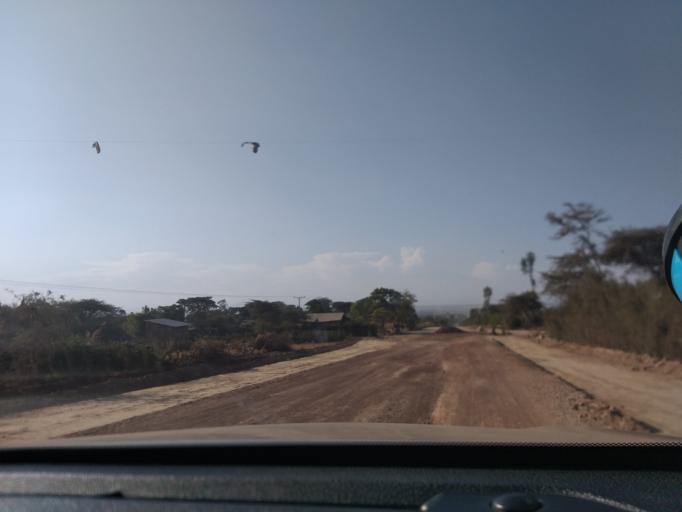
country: ET
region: Oromiya
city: Shashemene
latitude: 7.4422
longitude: 38.7703
